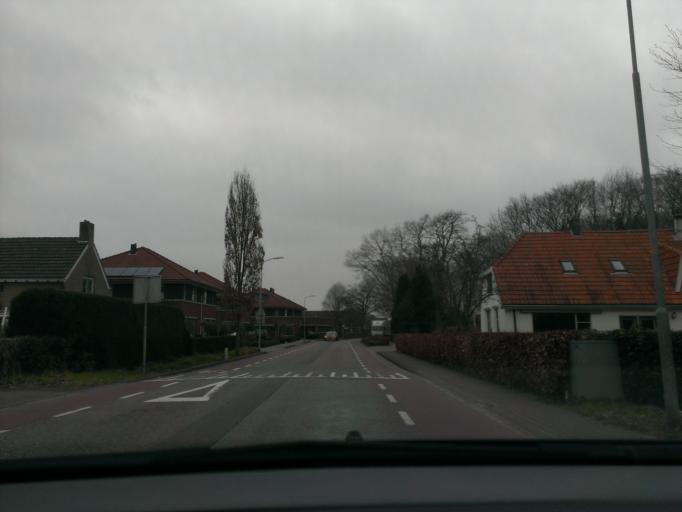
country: NL
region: Gelderland
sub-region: Gemeente Hattem
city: Hattem
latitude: 52.4738
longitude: 6.0532
